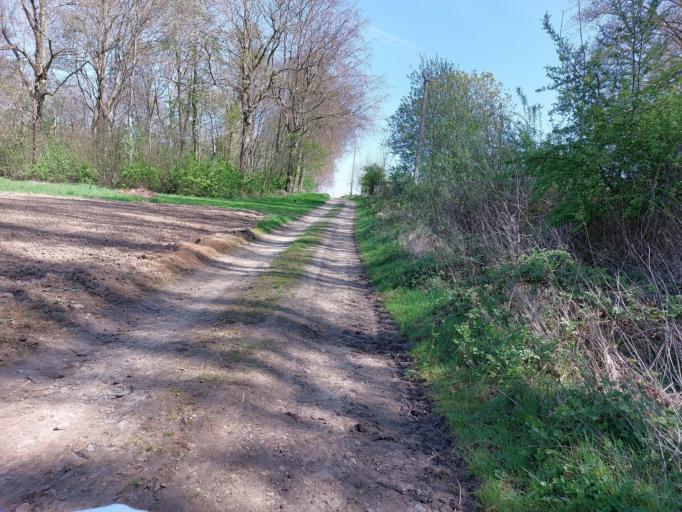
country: BE
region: Wallonia
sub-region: Province du Hainaut
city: Lens
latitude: 50.5897
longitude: 3.9588
